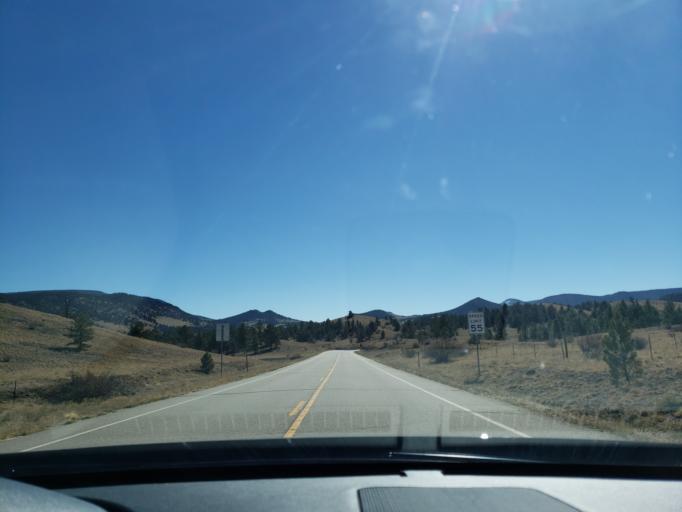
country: US
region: Colorado
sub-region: Chaffee County
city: Buena Vista
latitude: 38.8736
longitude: -105.6704
